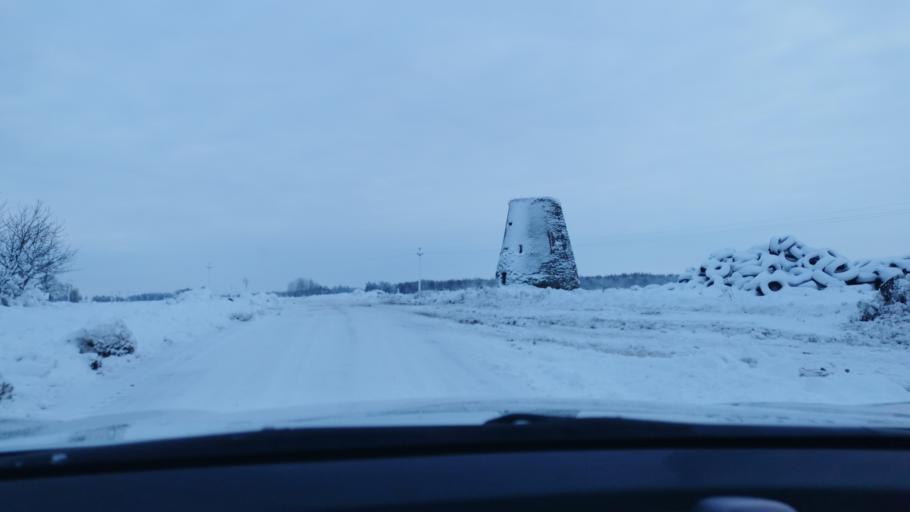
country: EE
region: Laeaene-Virumaa
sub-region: Haljala vald
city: Haljala
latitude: 59.5049
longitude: 26.2722
